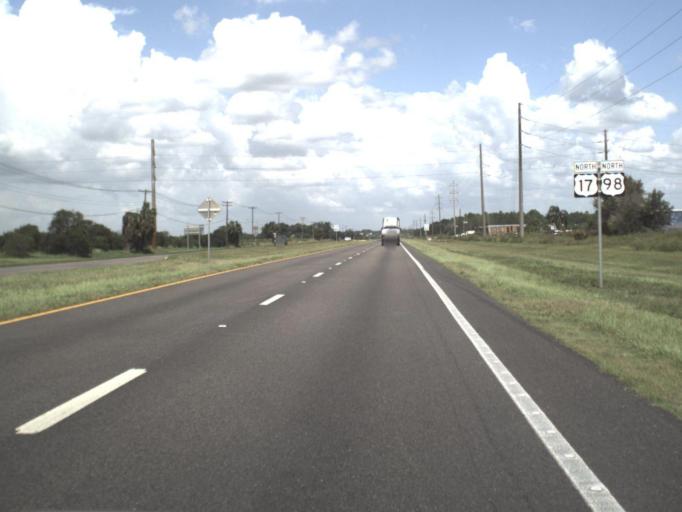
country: US
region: Florida
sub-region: Polk County
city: Fort Meade
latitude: 27.8216
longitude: -81.8217
